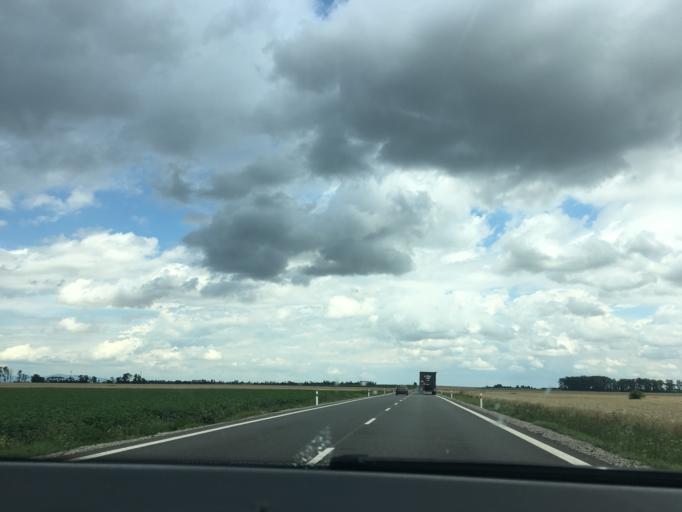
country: SK
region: Kosicky
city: Trebisov
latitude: 48.5539
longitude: 21.6947
